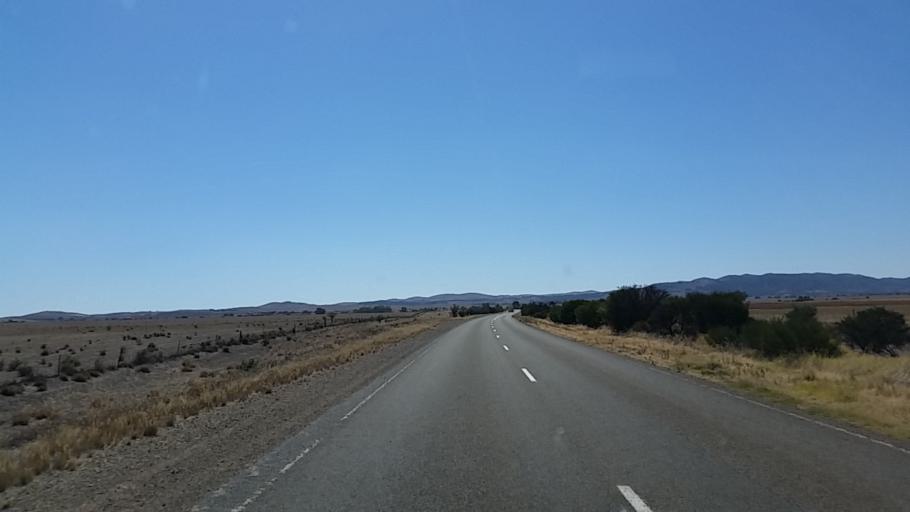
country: AU
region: South Australia
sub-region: Peterborough
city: Peterborough
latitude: -32.6493
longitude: 138.6011
